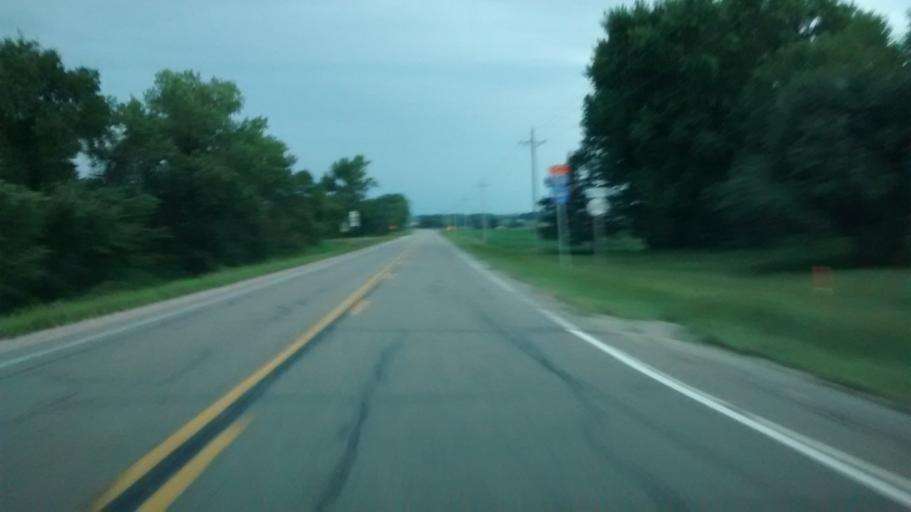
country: US
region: Iowa
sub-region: Woodbury County
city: Moville
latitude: 42.5036
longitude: -96.0647
